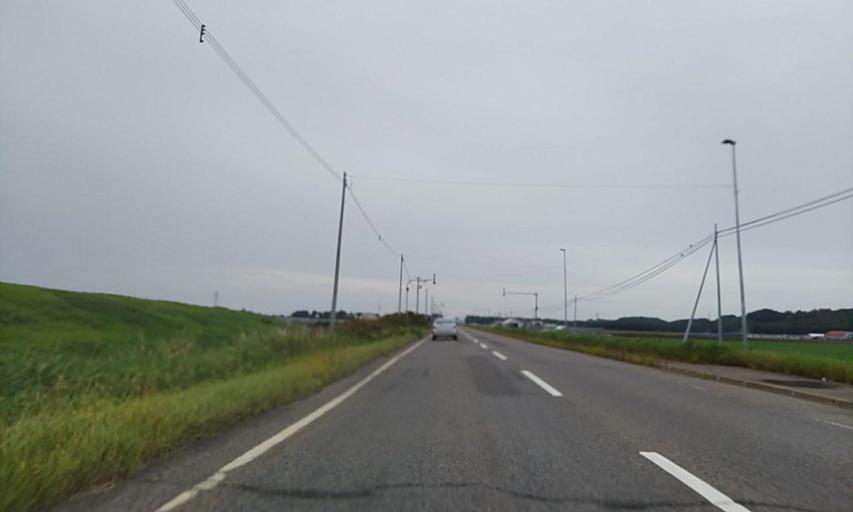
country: JP
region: Hokkaido
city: Bihoro
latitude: 43.8508
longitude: 144.1192
